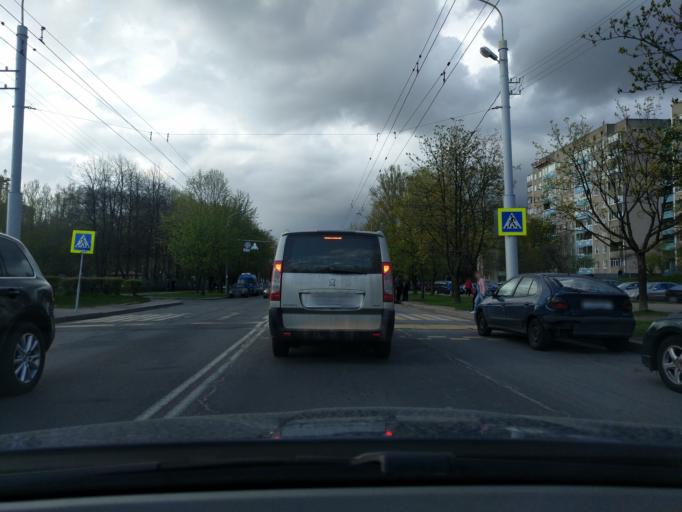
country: BY
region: Minsk
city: Novoye Medvezhino
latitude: 53.8957
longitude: 27.4813
